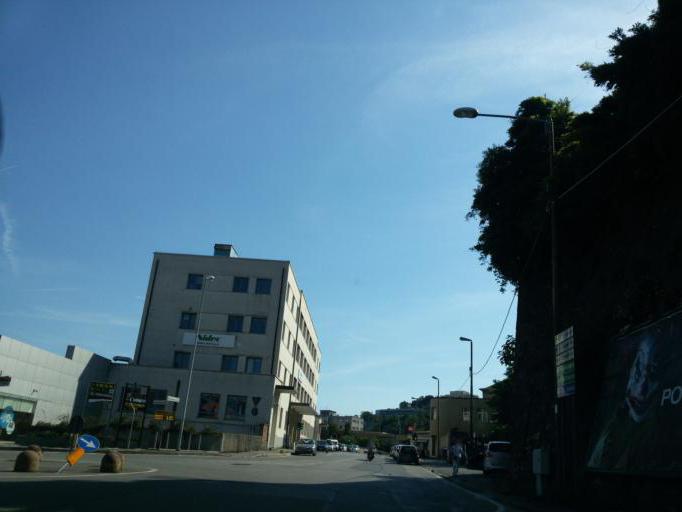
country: IT
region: Liguria
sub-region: Provincia di Genova
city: San Teodoro
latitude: 44.4244
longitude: 8.8824
